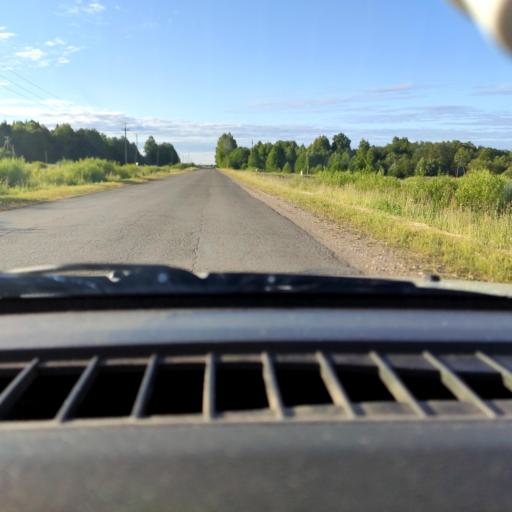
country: RU
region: Perm
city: Uinskoye
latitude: 57.0950
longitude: 56.5496
